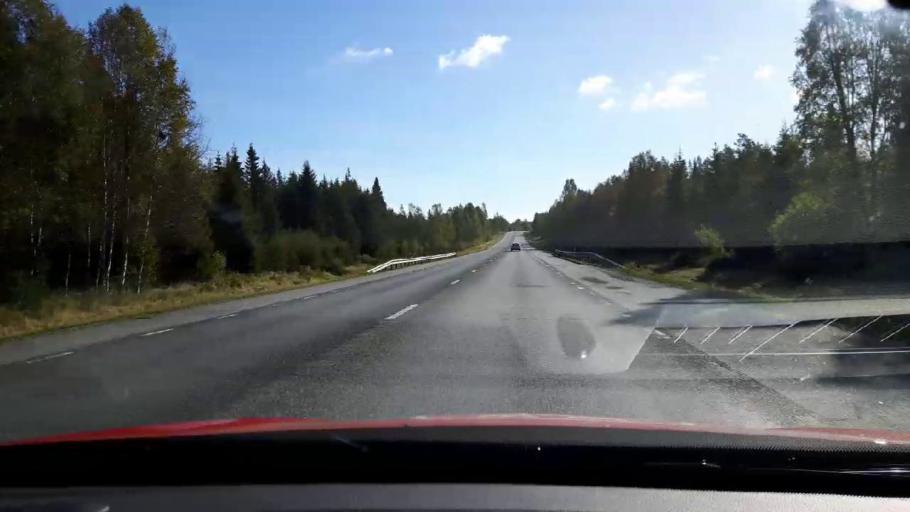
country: SE
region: Jaemtland
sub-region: Braecke Kommun
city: Braecke
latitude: 62.6884
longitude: 15.5617
